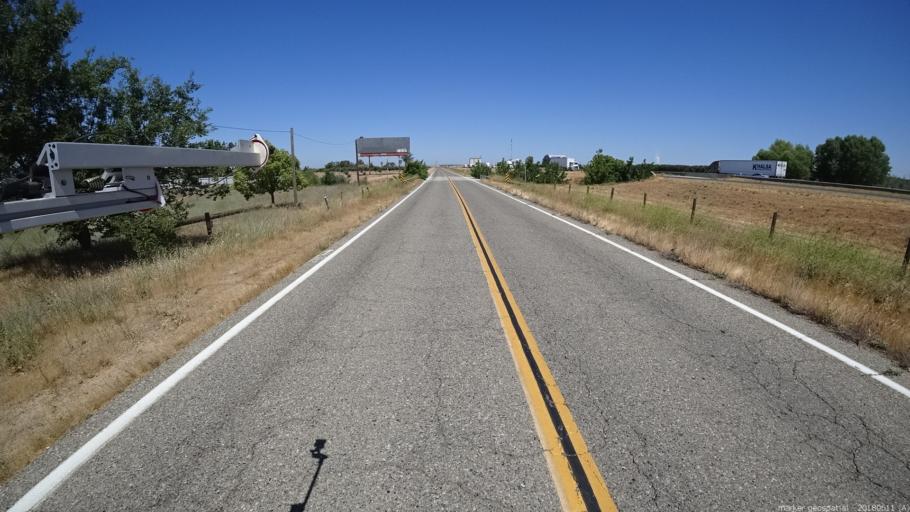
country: US
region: California
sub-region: Madera County
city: Fairmead
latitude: 37.0341
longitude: -120.1477
